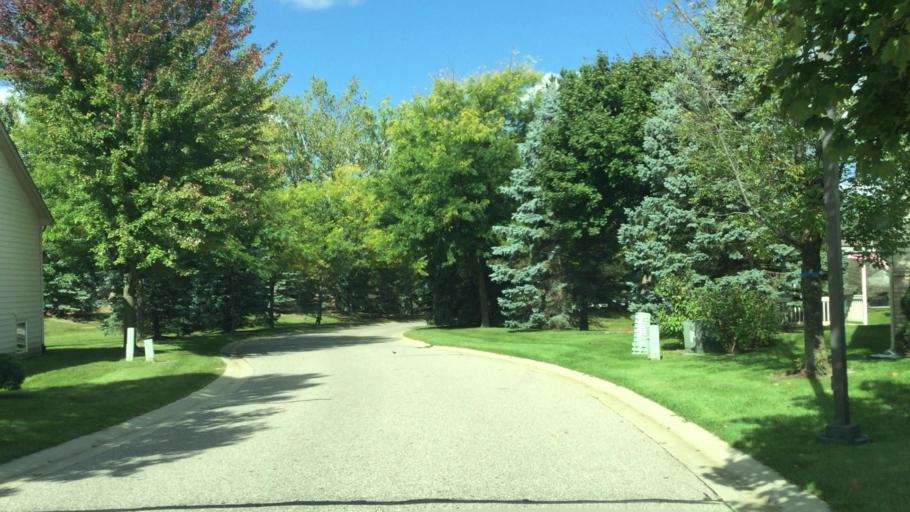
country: US
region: Michigan
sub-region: Genesee County
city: Grand Blanc
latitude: 42.9443
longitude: -83.6052
